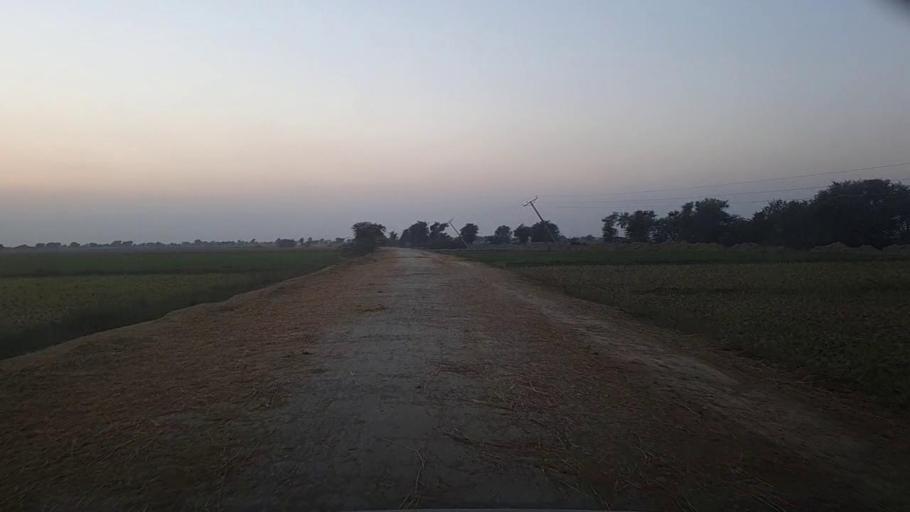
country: PK
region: Sindh
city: Khairpur Nathan Shah
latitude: 27.1811
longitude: 67.6079
